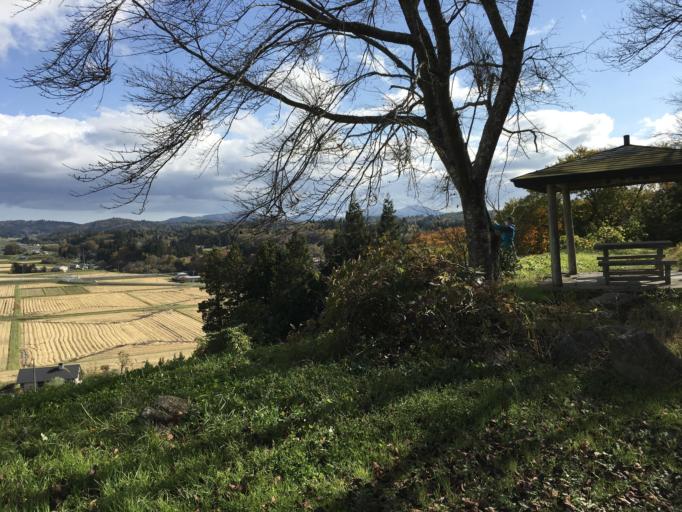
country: JP
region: Iwate
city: Ichinoseki
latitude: 38.9592
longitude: 141.3579
